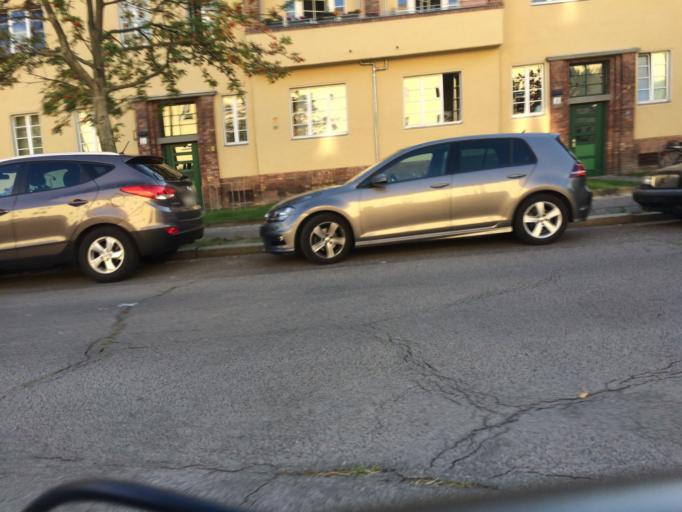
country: DE
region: Berlin
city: Heinersdorf
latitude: 52.5598
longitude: 13.4442
